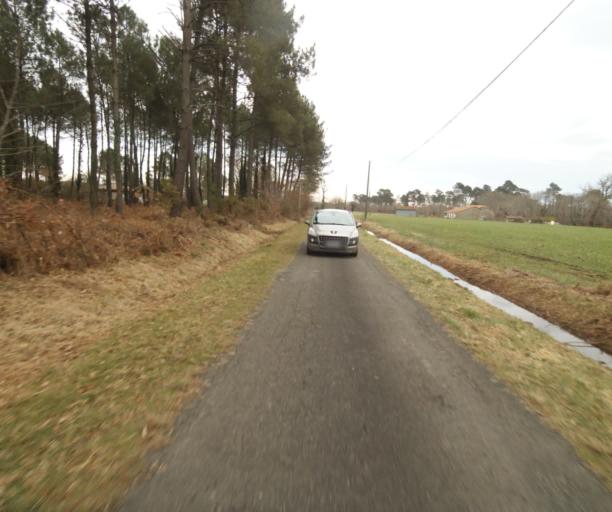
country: FR
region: Aquitaine
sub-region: Departement des Landes
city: Gabarret
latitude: 44.0197
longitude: -0.0656
